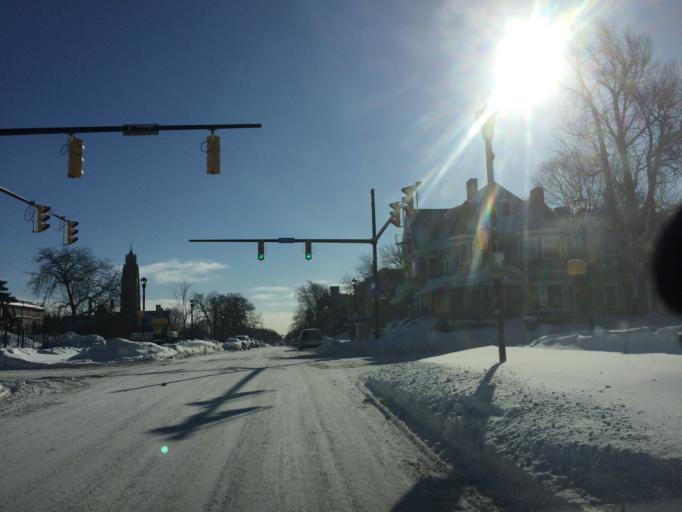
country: US
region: New York
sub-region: Monroe County
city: Rochester
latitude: 43.1578
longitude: -77.5911
